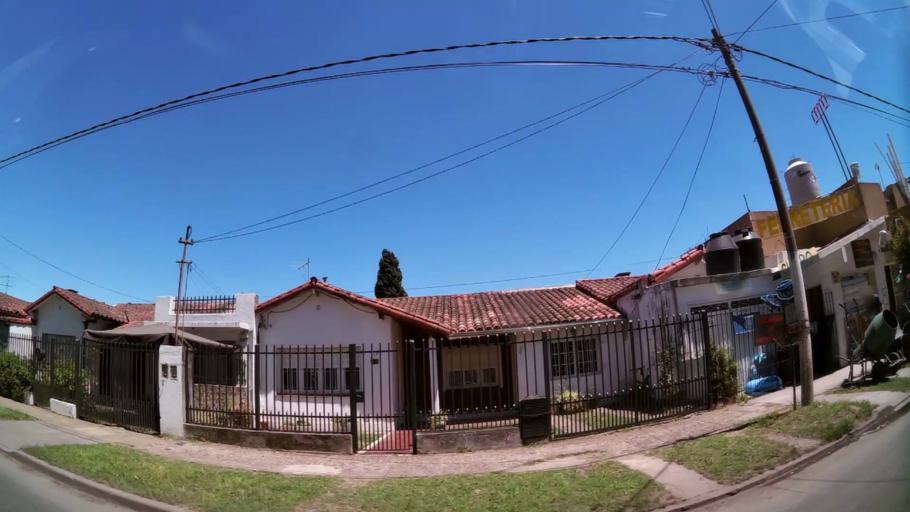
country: AR
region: Buenos Aires
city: Hurlingham
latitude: -34.5130
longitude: -58.7092
